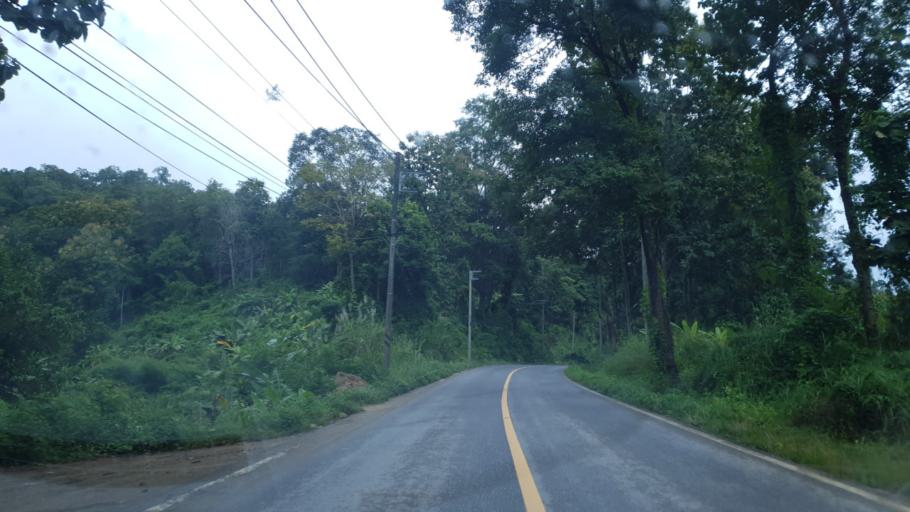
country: TH
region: Mae Hong Son
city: Ban Huai I Huak
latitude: 18.1386
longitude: 97.9906
